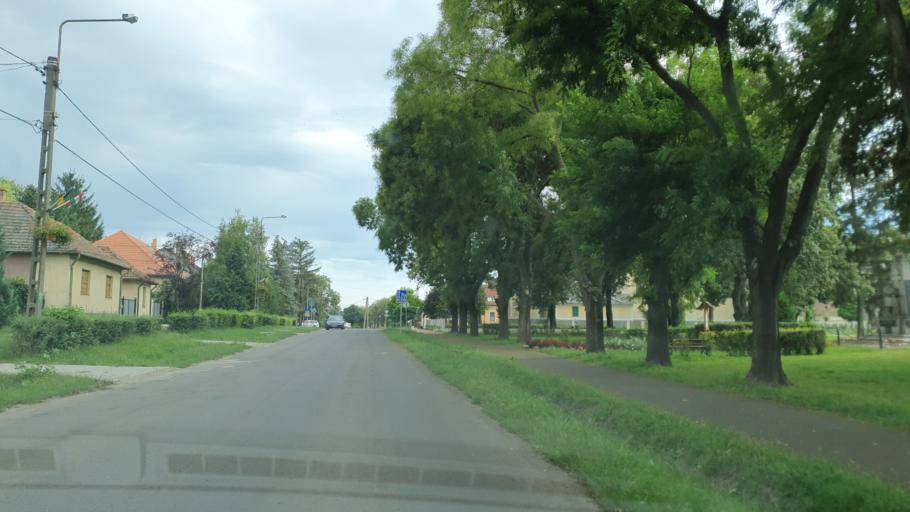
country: HU
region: Heves
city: Lorinci
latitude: 47.7396
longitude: 19.6786
